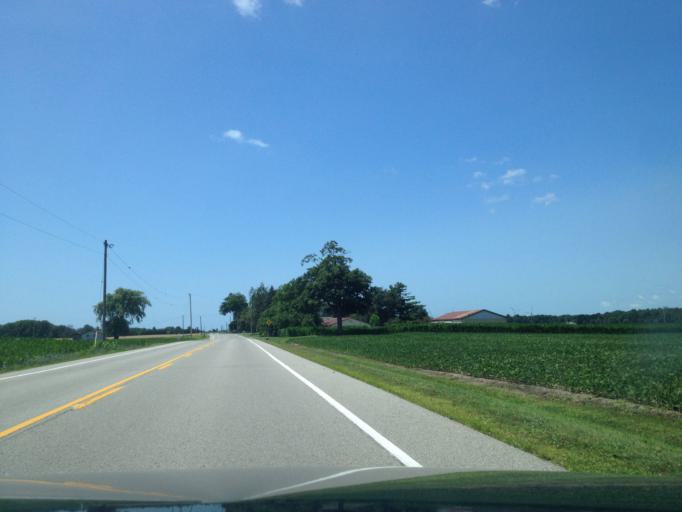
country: CA
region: Ontario
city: Norfolk County
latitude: 42.5899
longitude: -80.5063
